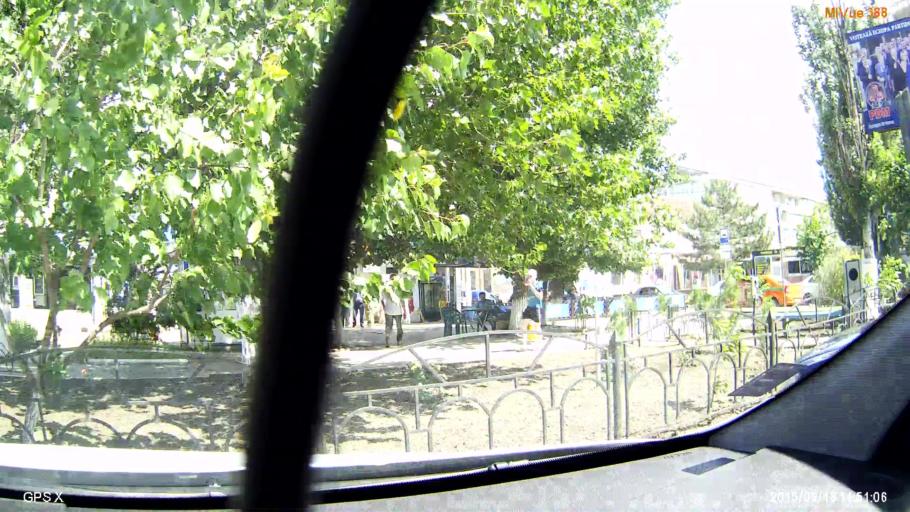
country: MD
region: Causeni
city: Causeni
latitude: 46.6427
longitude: 29.4089
